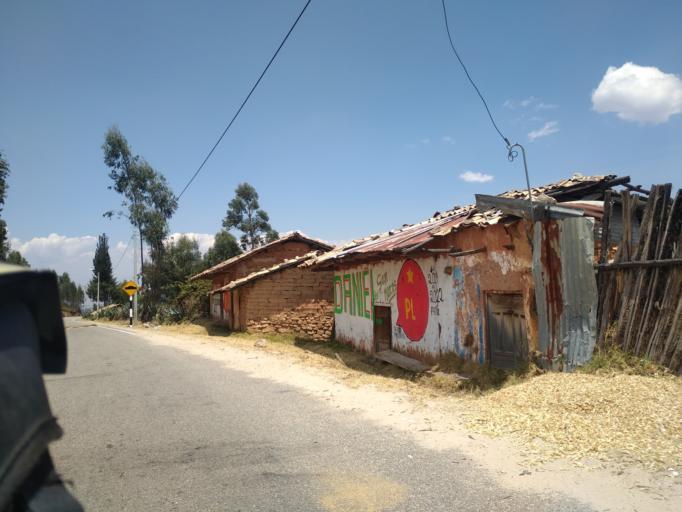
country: PE
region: Cajamarca
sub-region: San Marcos
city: San Marcos
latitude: -7.2834
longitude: -78.2166
